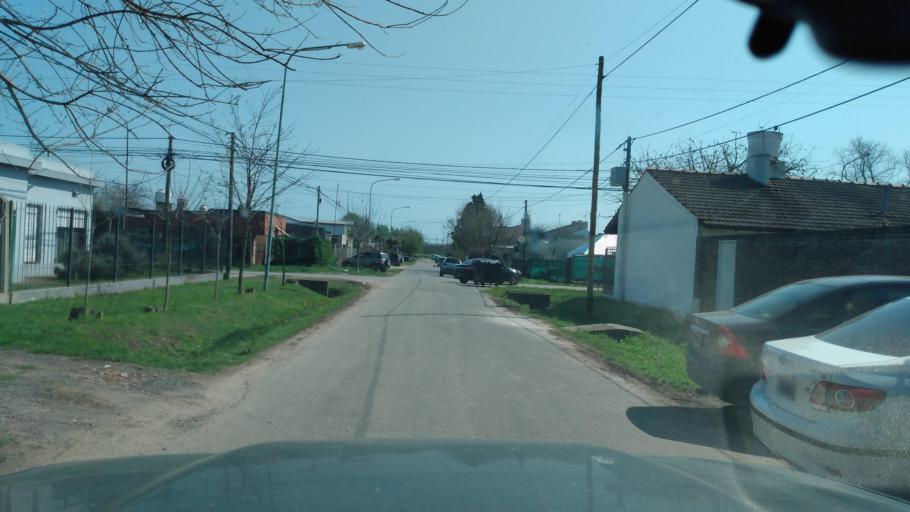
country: AR
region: Buenos Aires
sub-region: Partido de Lujan
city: Lujan
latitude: -34.5483
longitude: -59.1050
